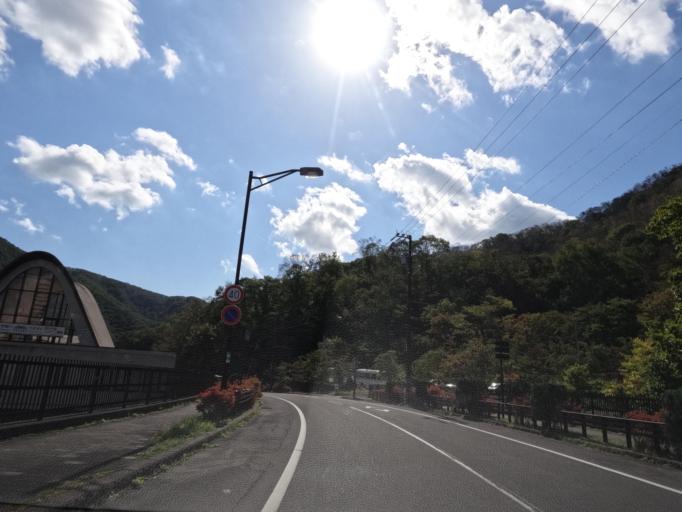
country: JP
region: Hokkaido
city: Shiraoi
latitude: 42.4914
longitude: 141.1427
